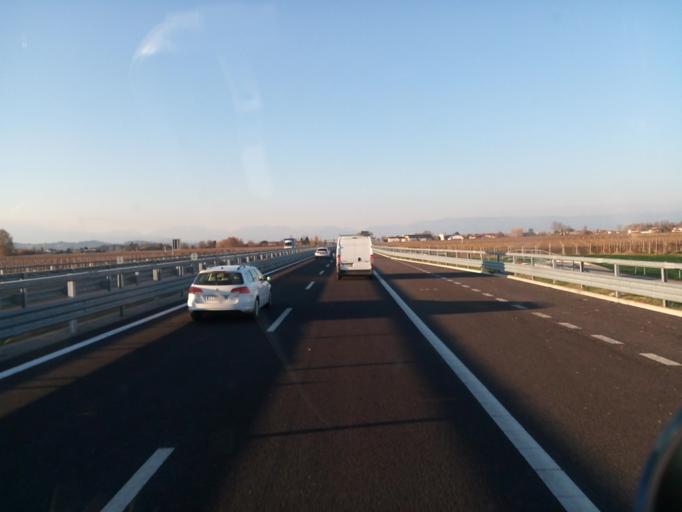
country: IT
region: Veneto
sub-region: Provincia di Vicenza
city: Longare
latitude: 45.4779
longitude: 11.6314
